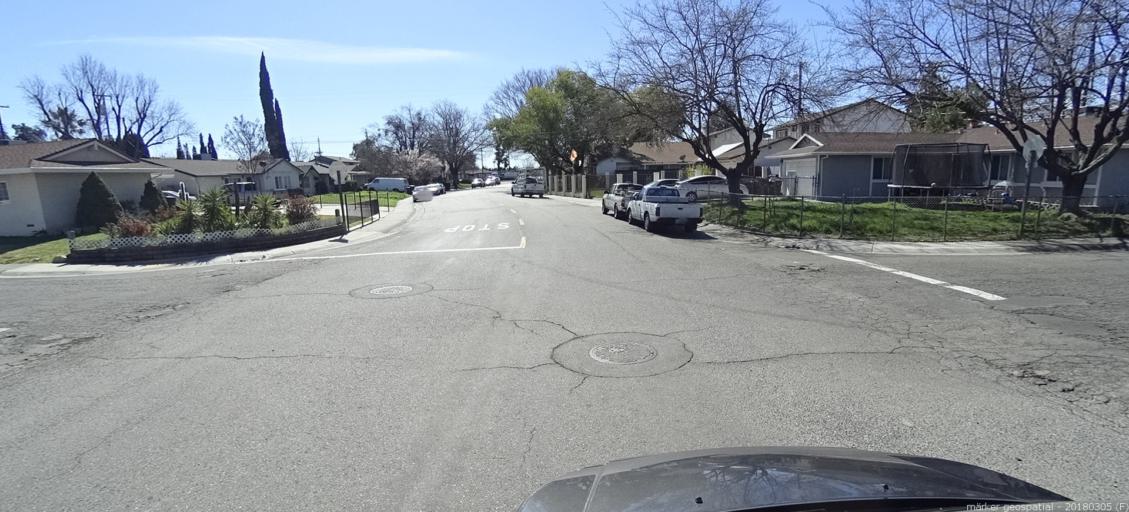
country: US
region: California
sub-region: Sacramento County
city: Florin
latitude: 38.4974
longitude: -121.4242
